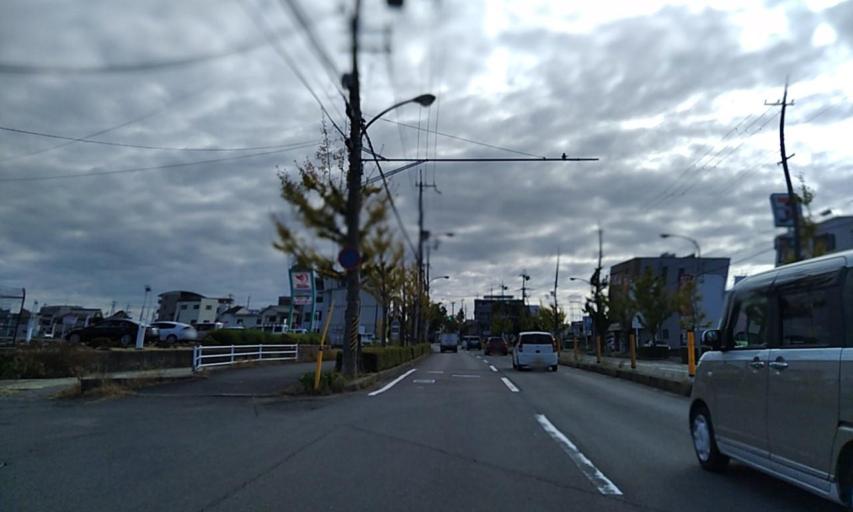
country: JP
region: Wakayama
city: Wakayama-shi
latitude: 34.2537
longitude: 135.1401
